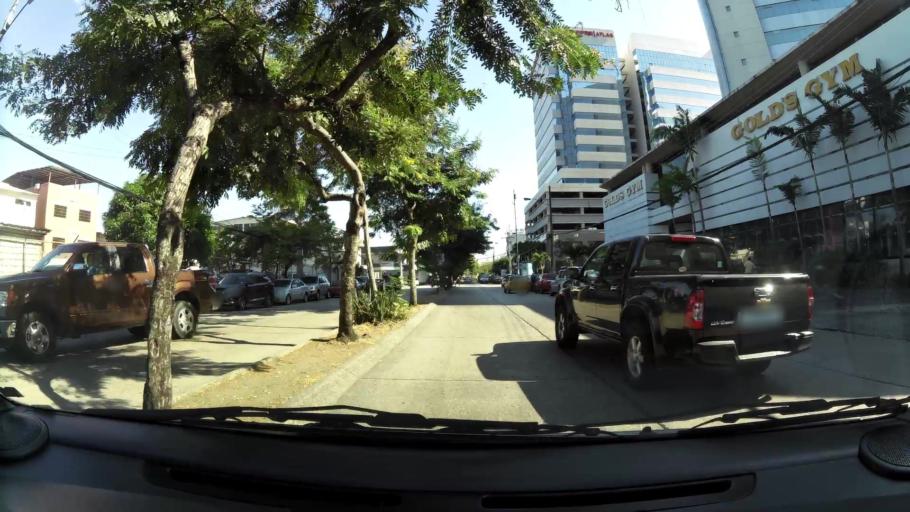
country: EC
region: Guayas
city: Guayaquil
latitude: -2.1631
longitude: -79.8985
